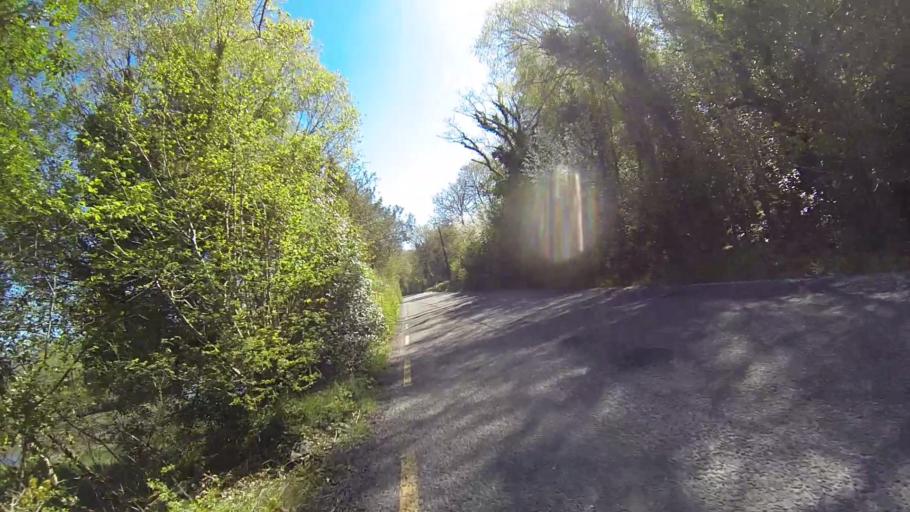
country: IE
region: Munster
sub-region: Ciarrai
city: Kenmare
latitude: 51.8421
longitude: -9.6746
